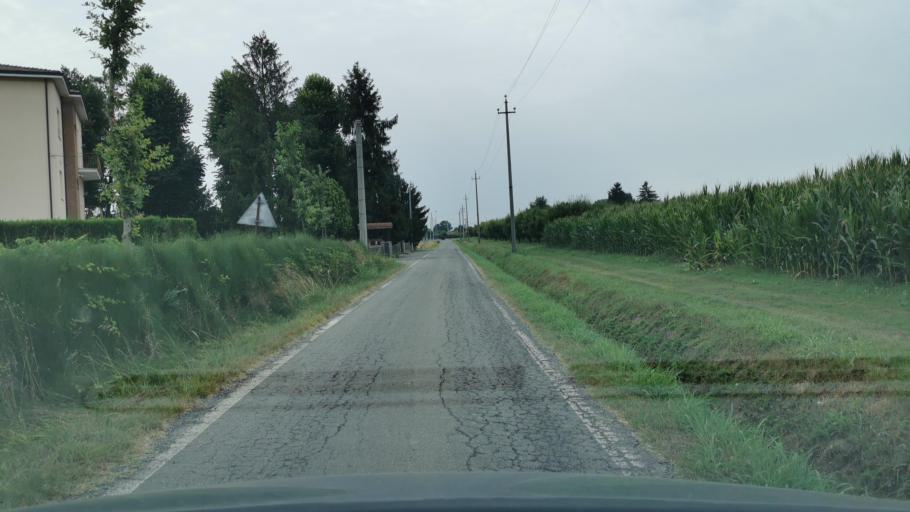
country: IT
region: Emilia-Romagna
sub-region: Provincia di Modena
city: Campogalliano
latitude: 44.6854
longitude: 10.8795
